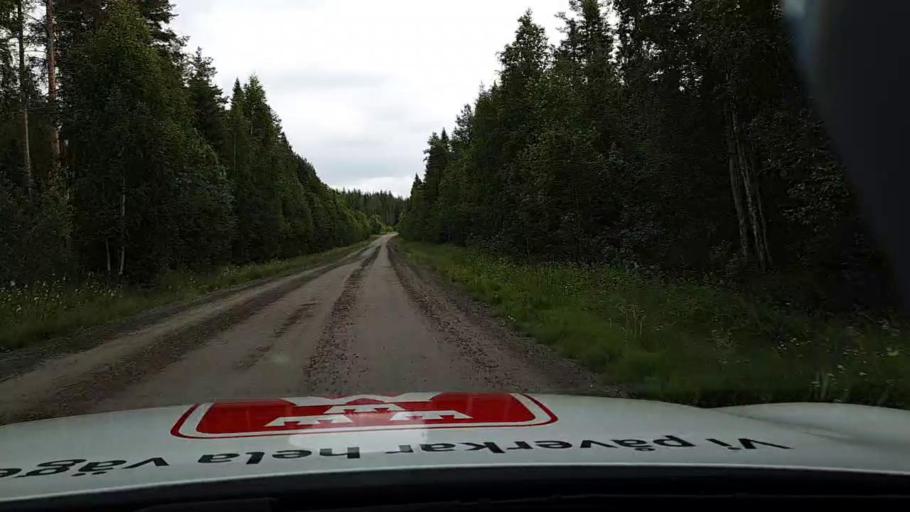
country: SE
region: Vaesternorrland
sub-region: Solleftea Kommun
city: As
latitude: 63.5112
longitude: 16.4004
